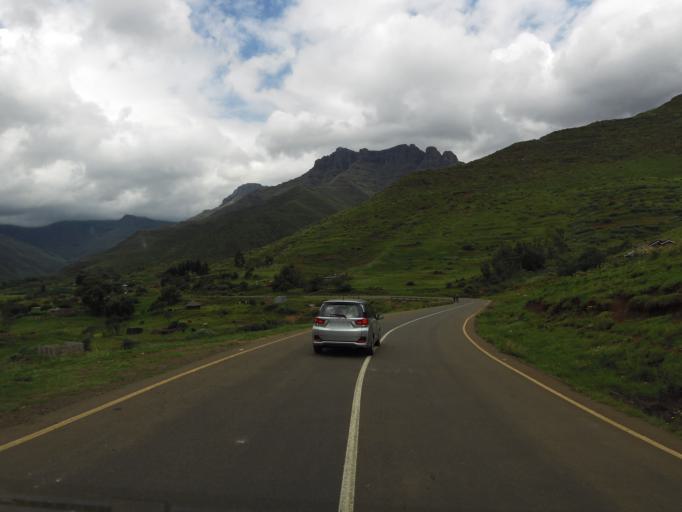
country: LS
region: Butha-Buthe
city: Butha-Buthe
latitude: -29.0474
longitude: 28.3239
